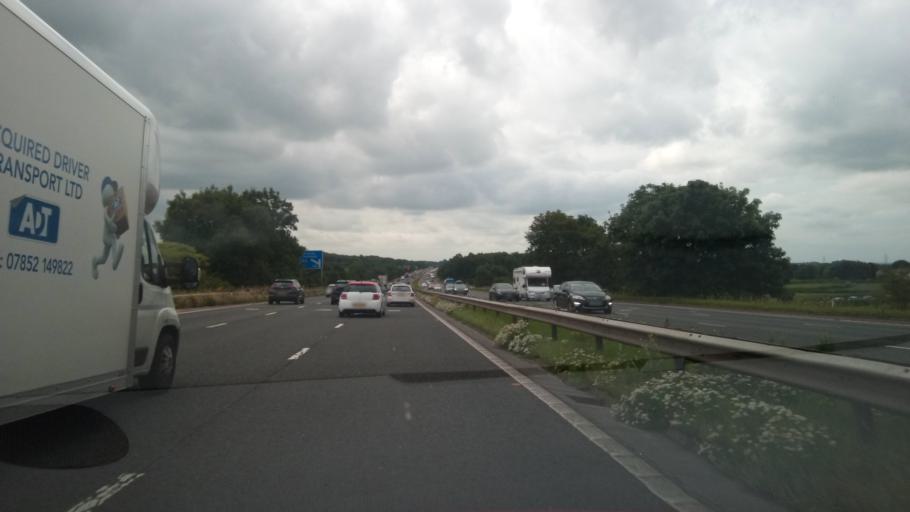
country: GB
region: England
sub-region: Lancashire
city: Galgate
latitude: 54.0063
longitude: -2.7806
